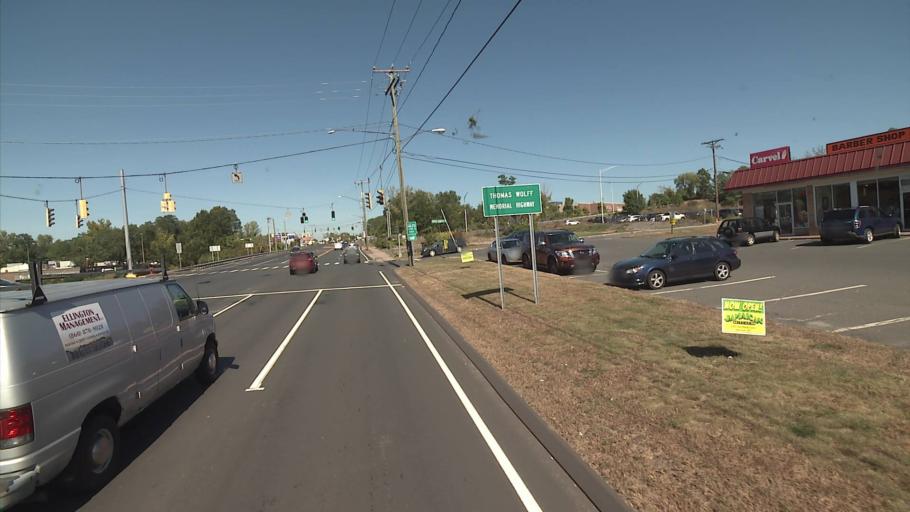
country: US
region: Connecticut
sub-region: Hartford County
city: Manchester
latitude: 41.8263
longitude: -72.4969
